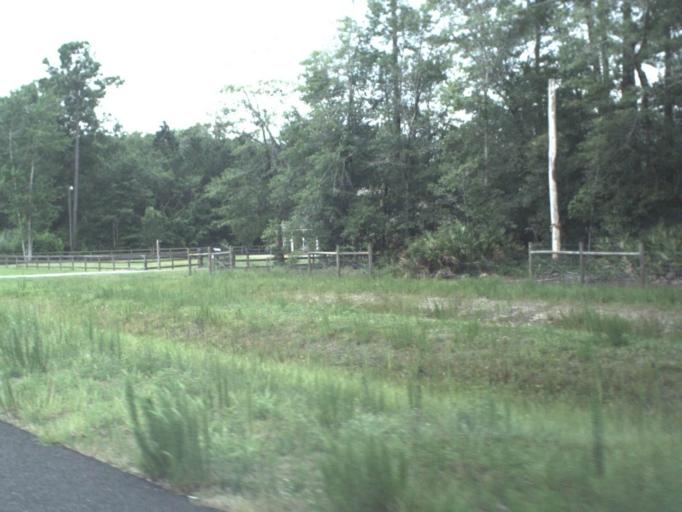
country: US
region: Florida
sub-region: Nassau County
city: Nassau Village-Ratliff
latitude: 30.4425
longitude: -81.9189
